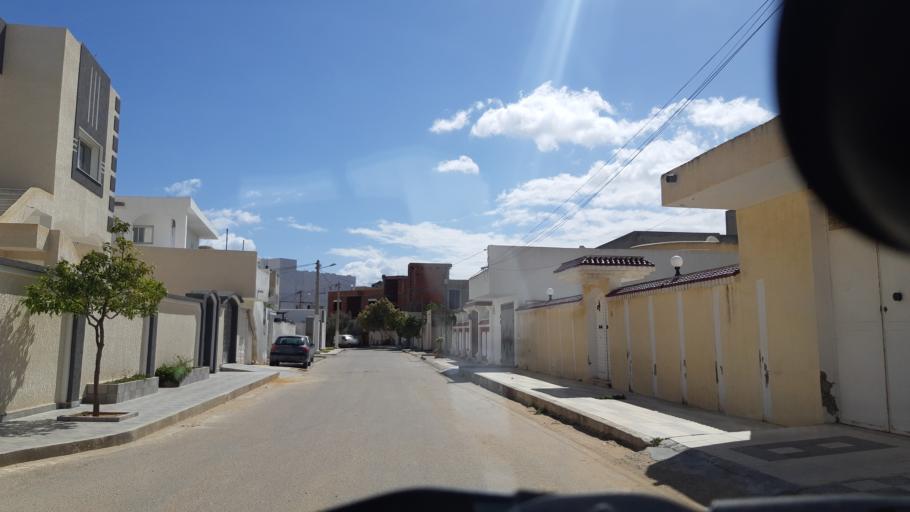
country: TN
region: Susah
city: Akouda
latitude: 35.8914
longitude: 10.5317
